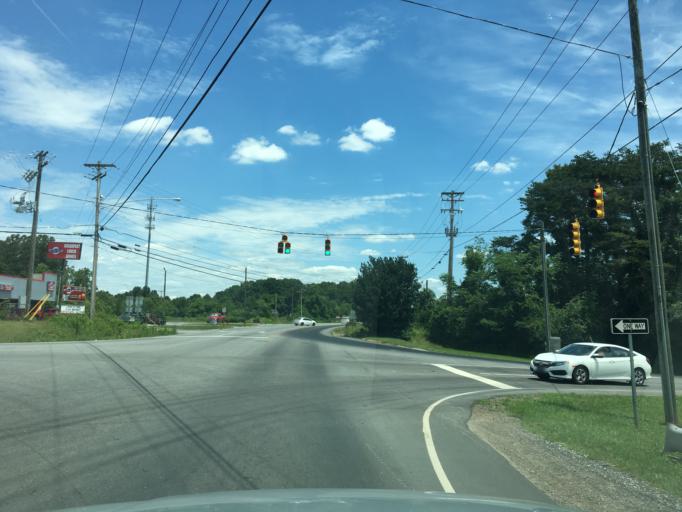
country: US
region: North Carolina
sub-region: Burke County
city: Glen Alpine
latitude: 35.7186
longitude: -81.7520
